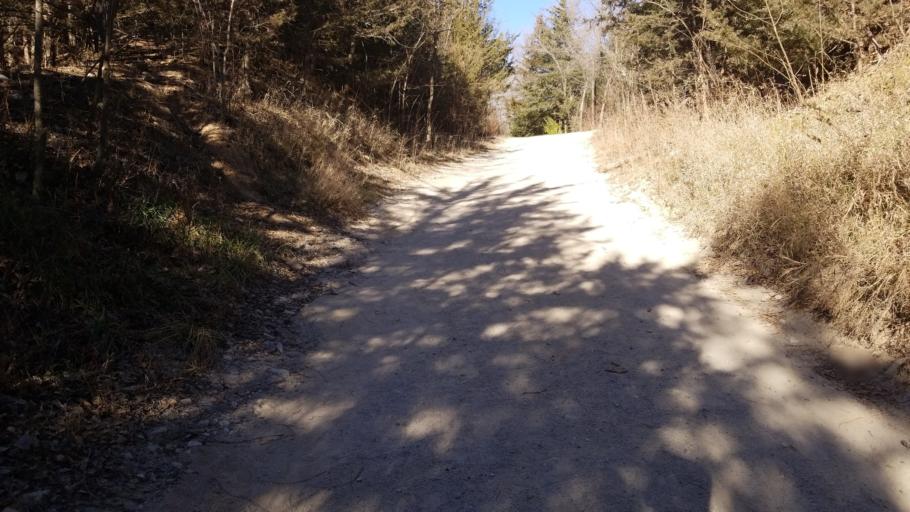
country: US
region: Nebraska
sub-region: Saunders County
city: Ashland
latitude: 41.0139
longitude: -96.2903
